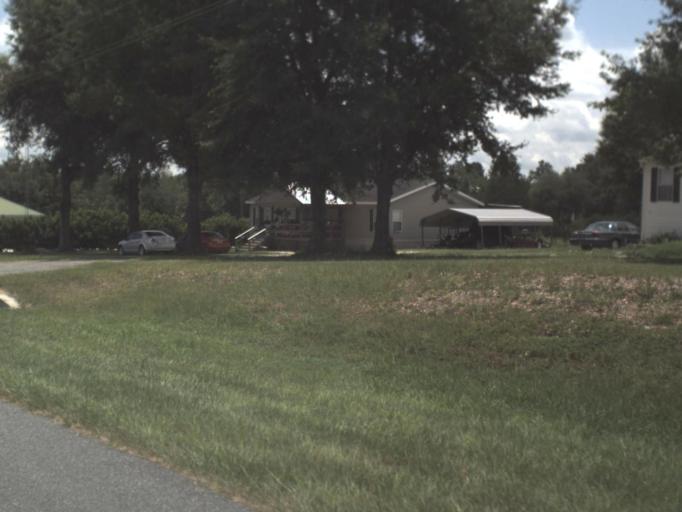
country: US
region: Florida
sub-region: Alachua County
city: High Springs
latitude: 30.0040
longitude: -82.5823
